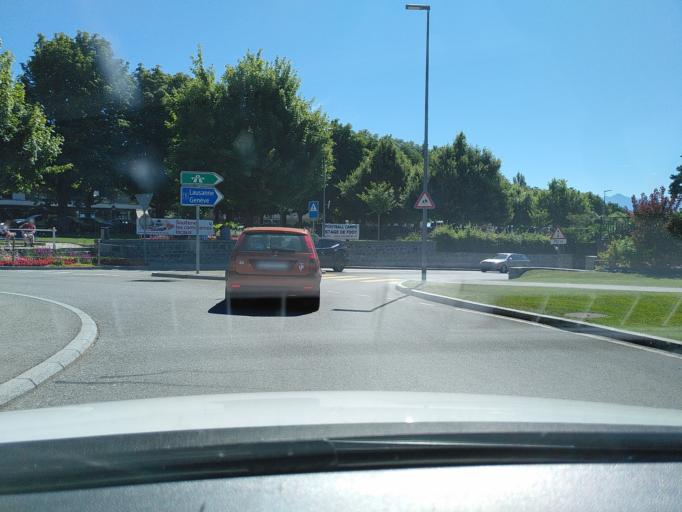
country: CH
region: Vaud
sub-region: Morges District
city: Aubonne
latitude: 46.4936
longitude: 6.3931
